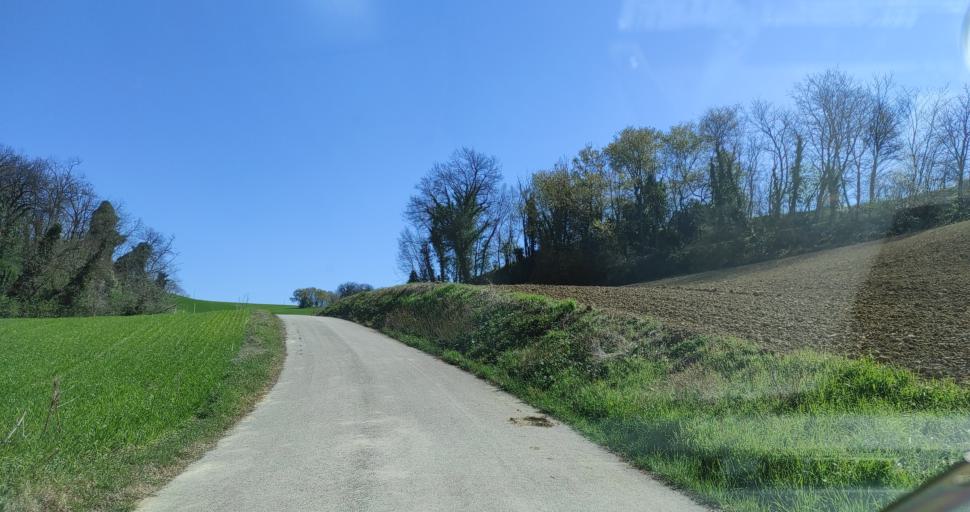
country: IT
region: The Marches
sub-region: Provincia di Macerata
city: Piediripa
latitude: 43.3135
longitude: 13.5012
